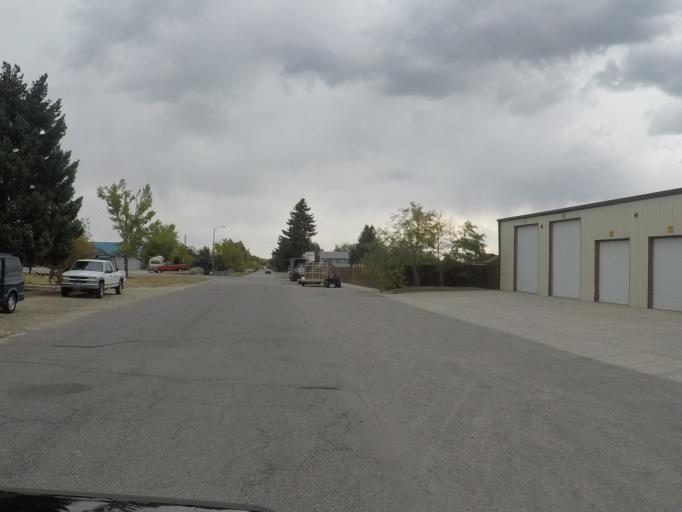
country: US
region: Montana
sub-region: Carbon County
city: Red Lodge
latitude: 45.1920
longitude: -109.2445
